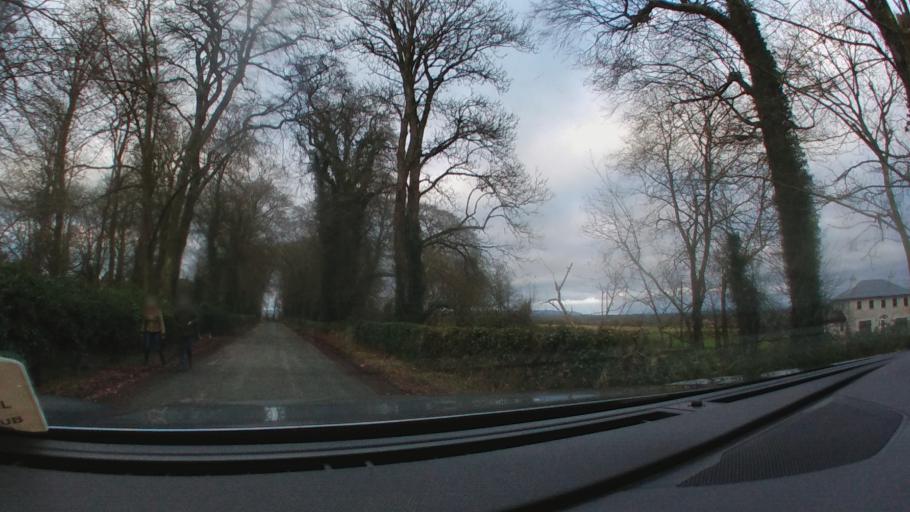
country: IE
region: Leinster
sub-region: Kilkenny
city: Thomastown
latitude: 52.5620
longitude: -7.1395
